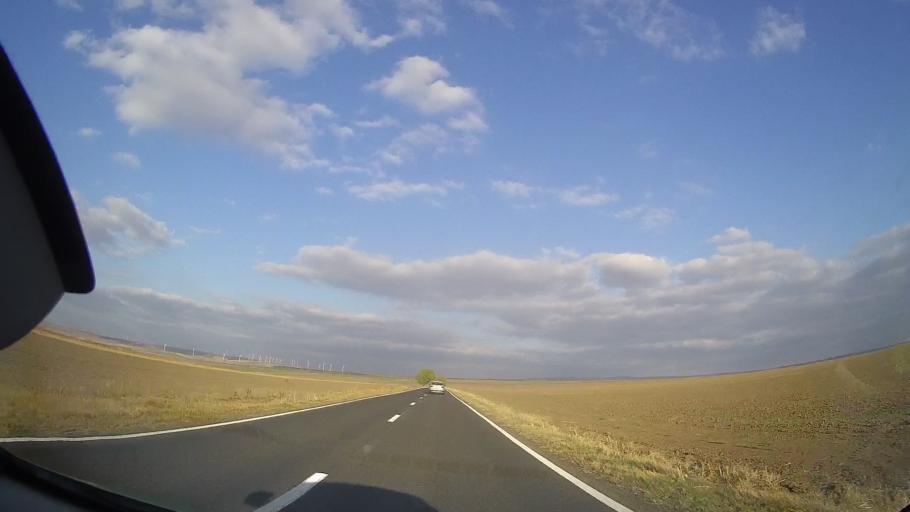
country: RO
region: Tulcea
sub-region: Comuna Topolog
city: Topolog
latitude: 44.8351
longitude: 28.2929
